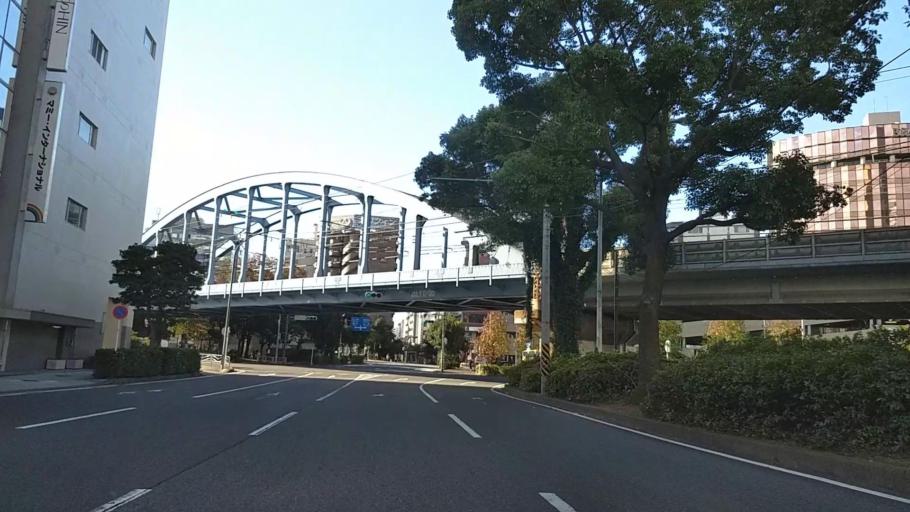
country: JP
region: Kanagawa
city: Yokohama
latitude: 35.4491
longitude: 139.6325
